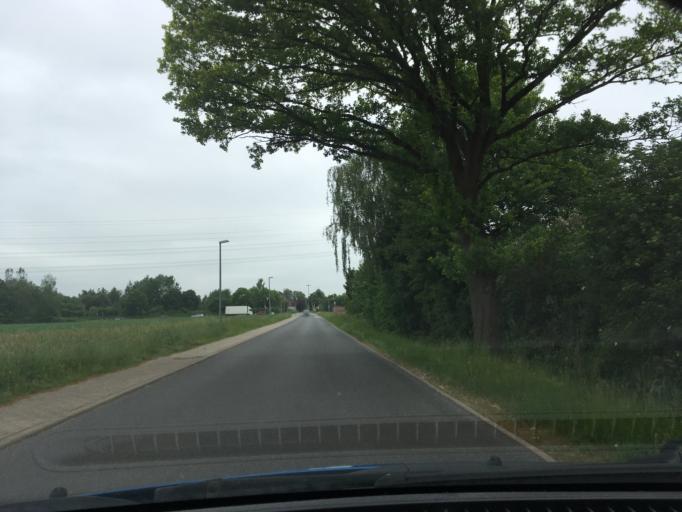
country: DE
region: Lower Saxony
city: Winsen
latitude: 53.3433
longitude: 10.2225
